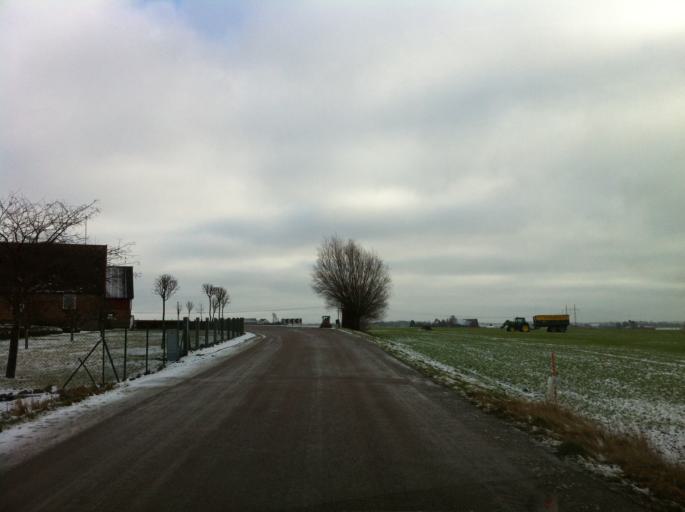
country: SE
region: Skane
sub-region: Svalovs Kommun
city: Teckomatorp
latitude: 55.8740
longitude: 13.0421
